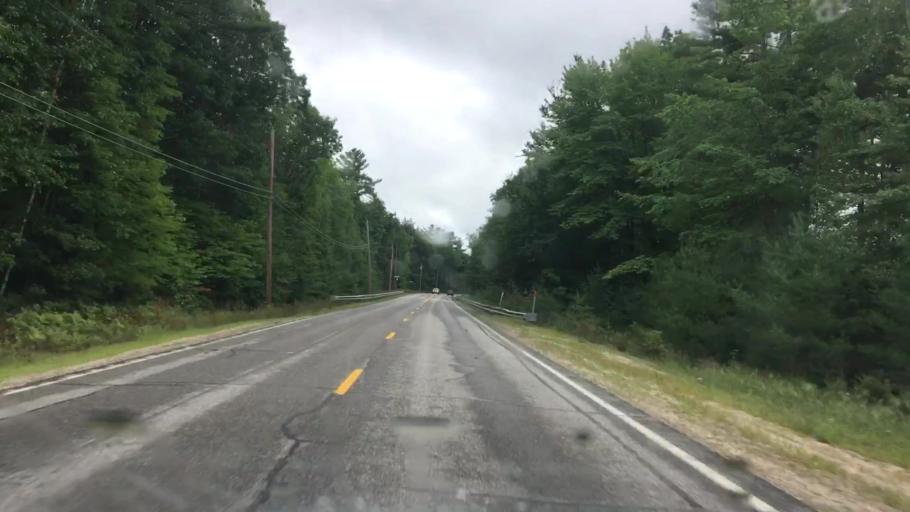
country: US
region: Maine
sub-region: Oxford County
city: Fryeburg
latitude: 44.0045
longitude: -70.9493
